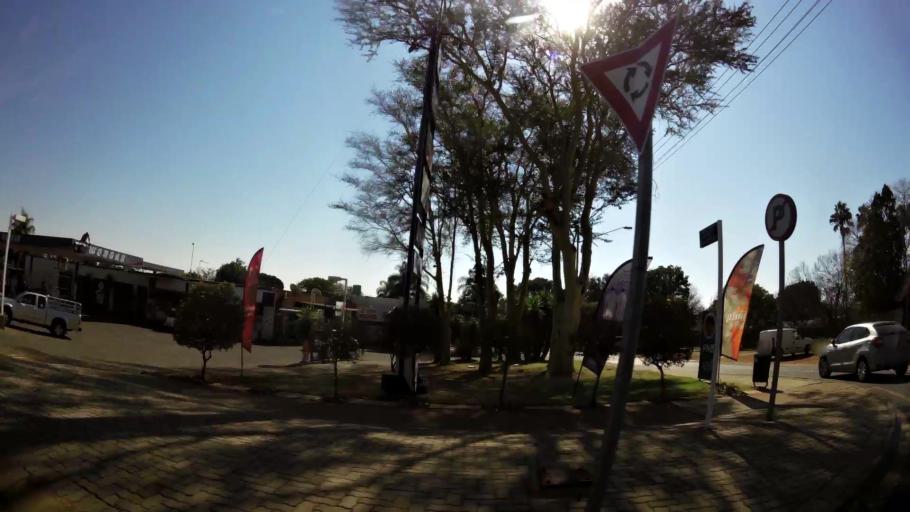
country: ZA
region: Gauteng
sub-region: City of Tshwane Metropolitan Municipality
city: Pretoria
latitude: -25.6838
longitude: 28.2040
